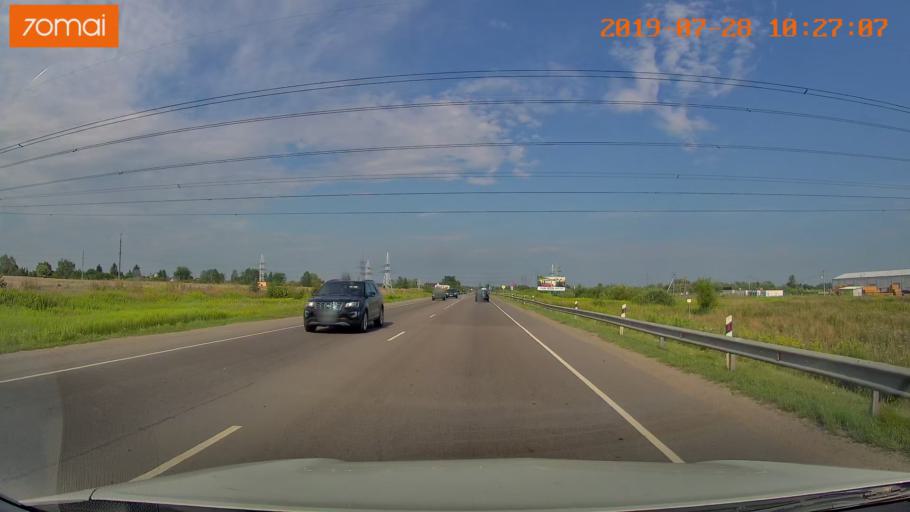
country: RU
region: Kaliningrad
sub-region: Gorod Kaliningrad
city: Kaliningrad
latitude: 54.7698
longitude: 20.5232
